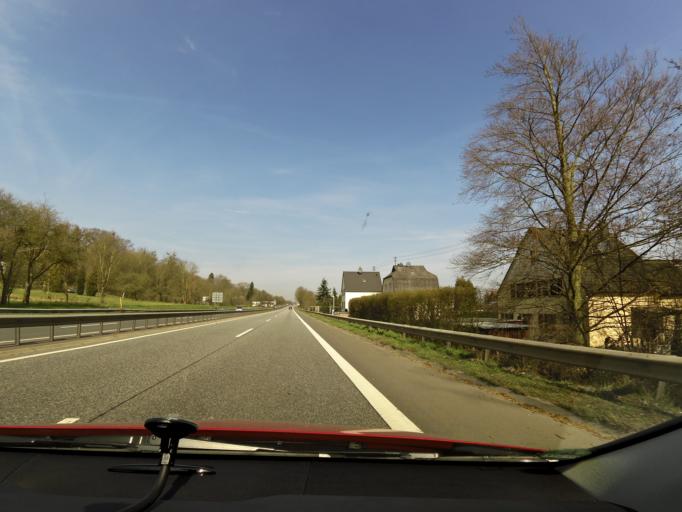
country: DE
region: Rheinland-Pfalz
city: Sinzig
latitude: 50.5375
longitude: 7.2656
